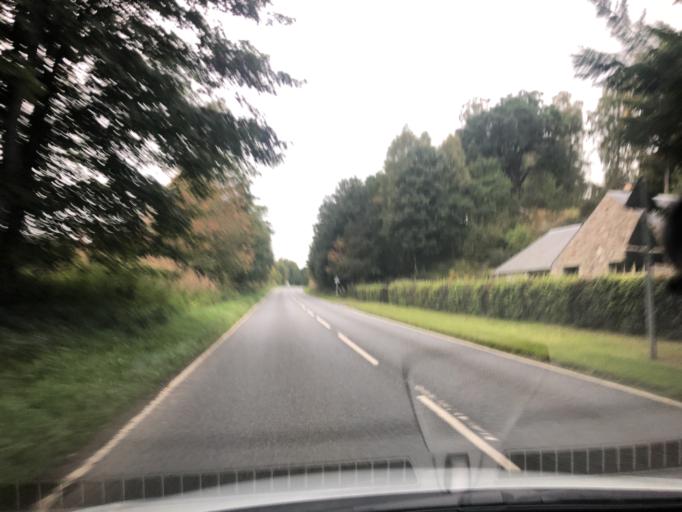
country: GB
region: Scotland
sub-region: Perth and Kinross
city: Pitlochry
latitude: 56.7489
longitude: -3.7923
